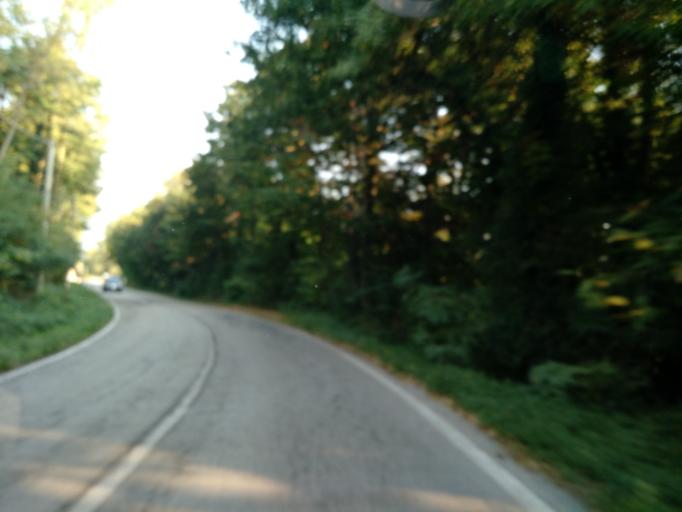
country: IT
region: Veneto
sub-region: Provincia di Vicenza
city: Salcedo
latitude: 45.7409
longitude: 11.5629
